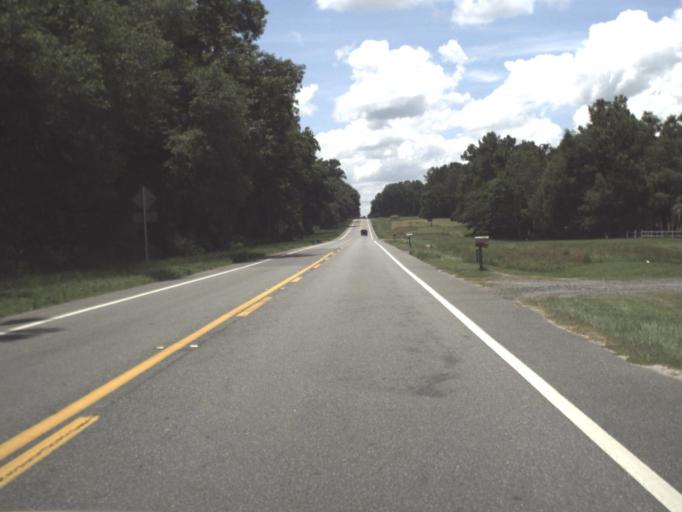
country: US
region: Florida
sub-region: Columbia County
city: Five Points
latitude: 30.2984
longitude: -82.7081
